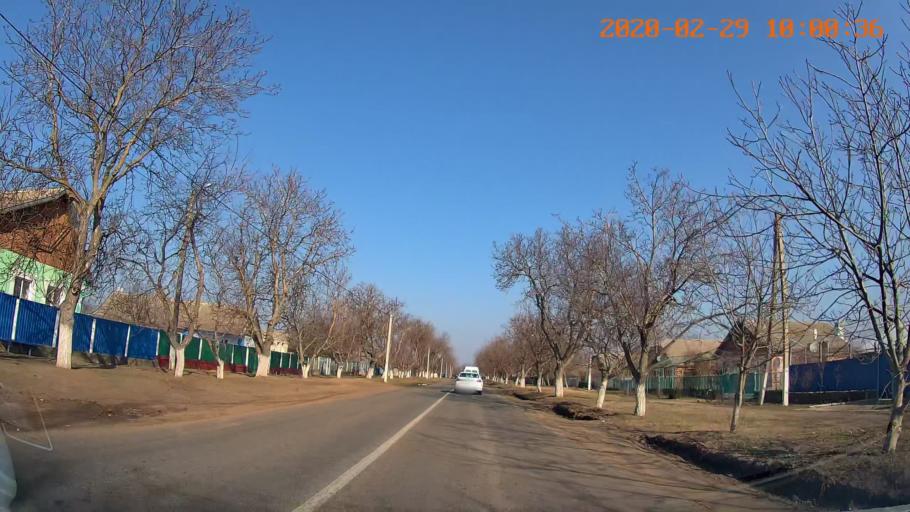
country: MD
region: Telenesti
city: Slobozia
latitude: 46.7695
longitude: 29.6861
